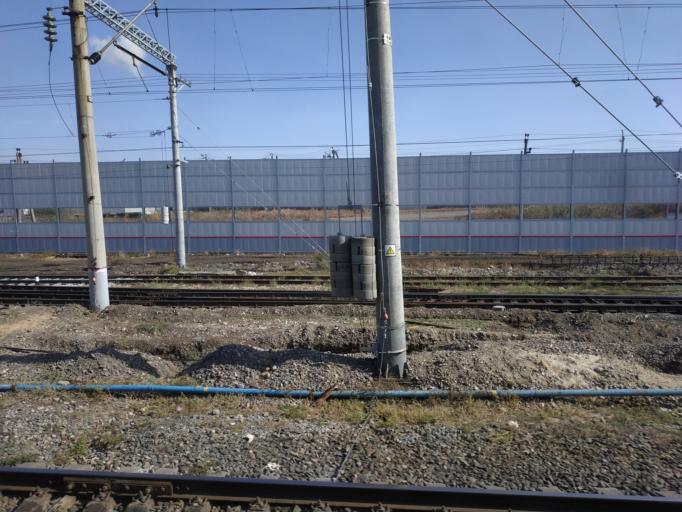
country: RU
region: Volgograd
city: Gumrak
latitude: 48.7772
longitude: 44.3801
